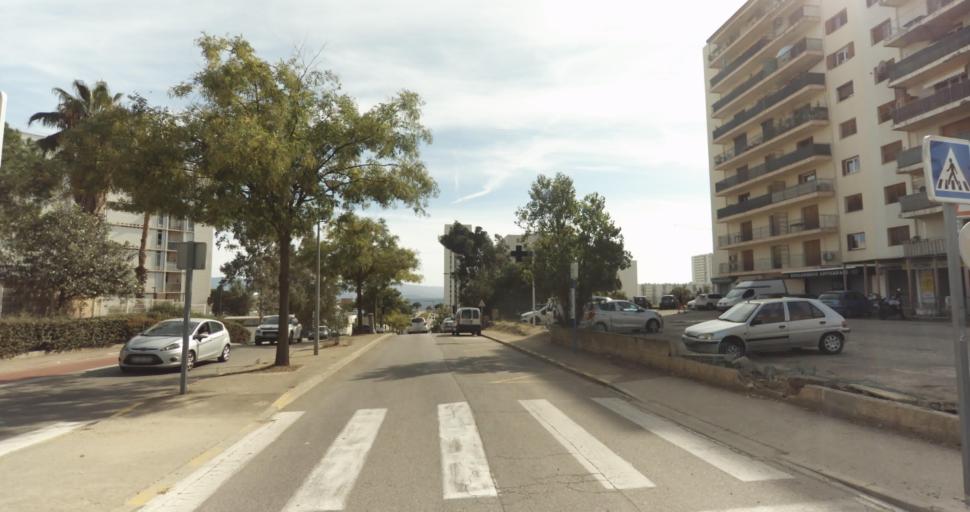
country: FR
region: Corsica
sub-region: Departement de la Corse-du-Sud
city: Ajaccio
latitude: 41.9392
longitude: 8.7508
